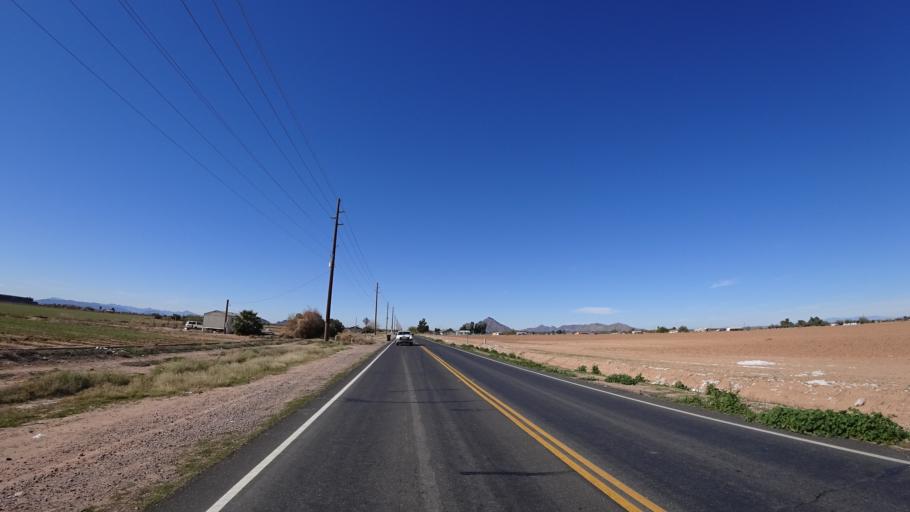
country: US
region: Arizona
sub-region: Maricopa County
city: Scottsdale
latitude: 33.4950
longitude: -111.8584
